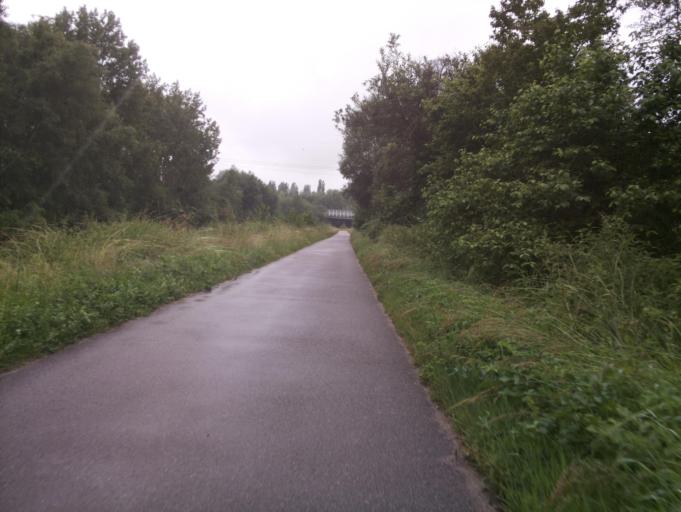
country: FR
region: Picardie
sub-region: Departement de la Somme
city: Dreuil-les-Amiens
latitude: 49.9176
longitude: 2.2383
